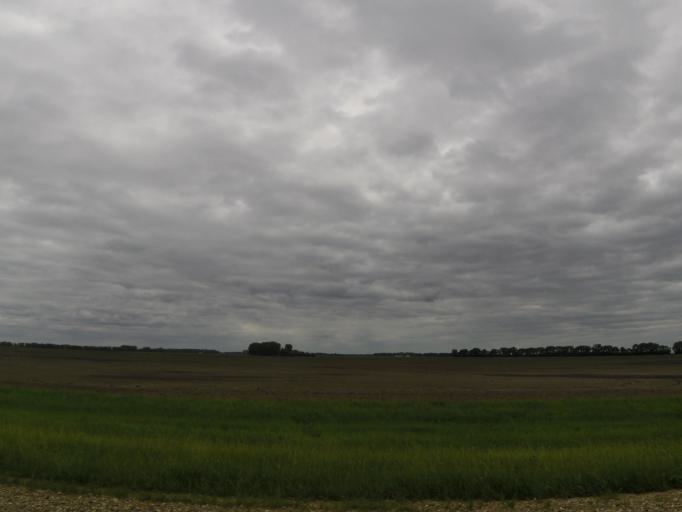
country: US
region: North Dakota
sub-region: Walsh County
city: Grafton
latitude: 48.6262
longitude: -97.4522
